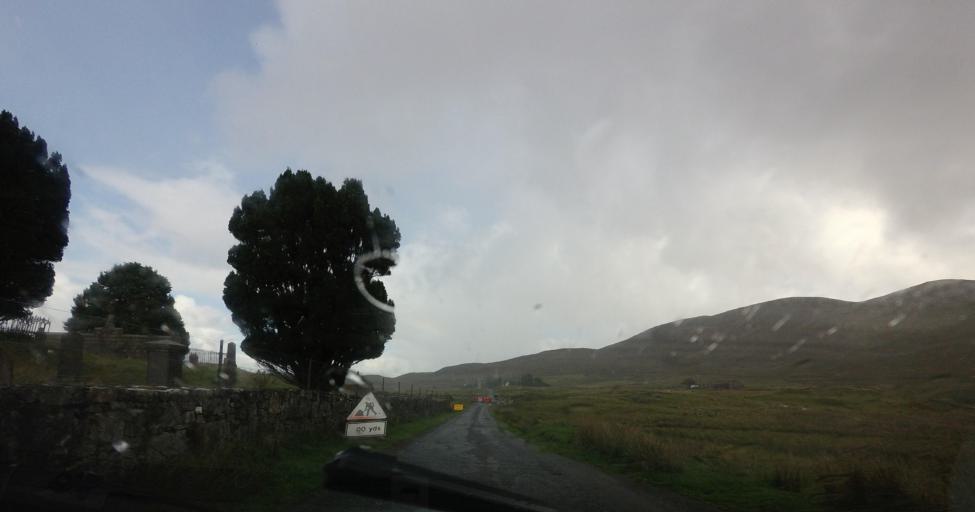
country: GB
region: Scotland
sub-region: Highland
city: Portree
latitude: 57.2148
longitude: -5.9477
